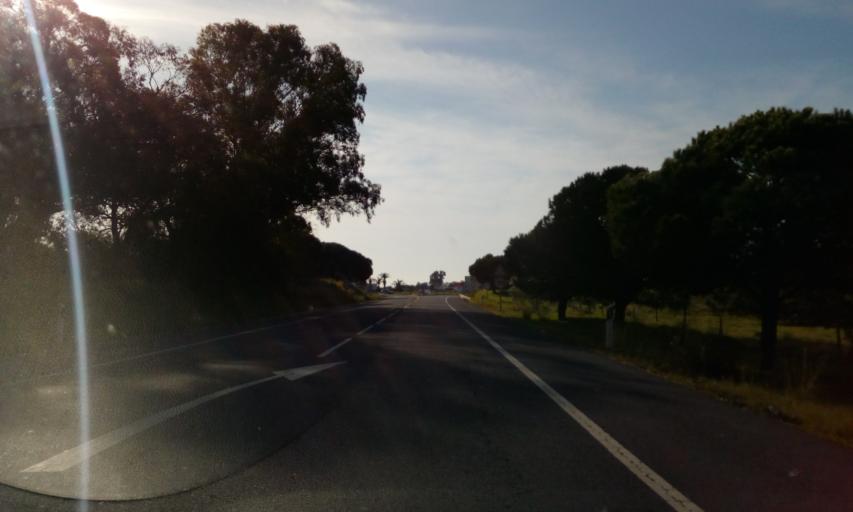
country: PT
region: Faro
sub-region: Vila Real de Santo Antonio
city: Monte Gordo
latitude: 37.1843
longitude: -7.4914
